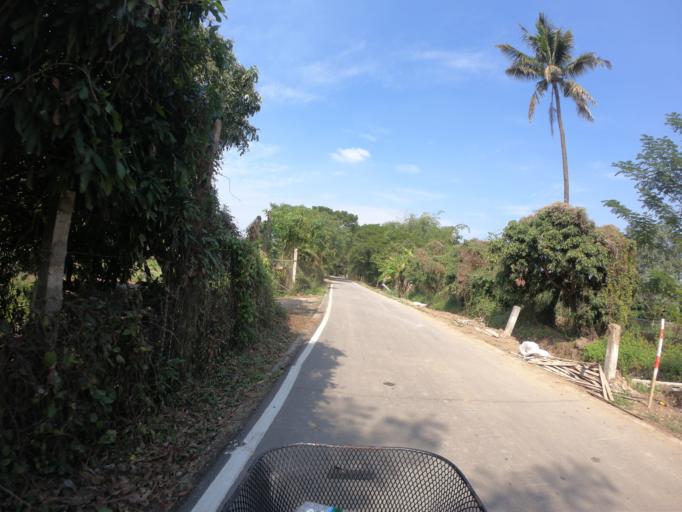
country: TH
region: Chiang Mai
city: Saraphi
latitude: 18.7002
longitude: 99.0565
